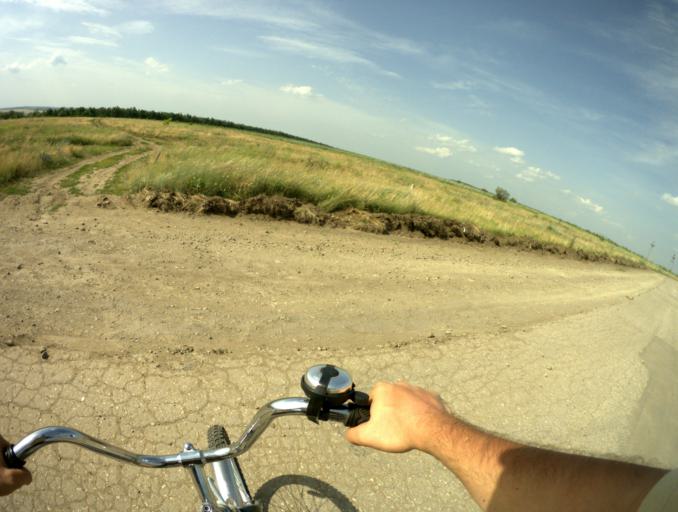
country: RU
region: Saratov
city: Yelshanka
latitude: 51.8197
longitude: 46.5002
